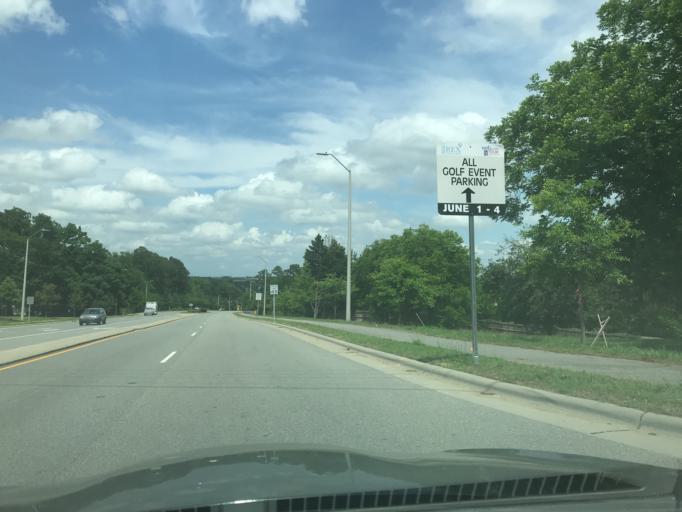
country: US
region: North Carolina
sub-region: Wake County
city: Wake Forest
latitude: 35.9323
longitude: -78.5805
